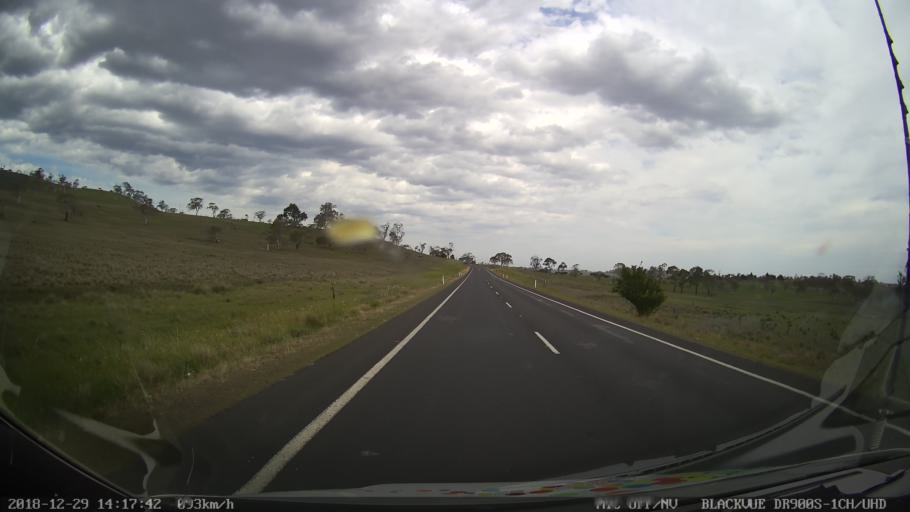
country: AU
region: New South Wales
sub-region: Cooma-Monaro
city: Cooma
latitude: -36.4821
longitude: 149.2603
